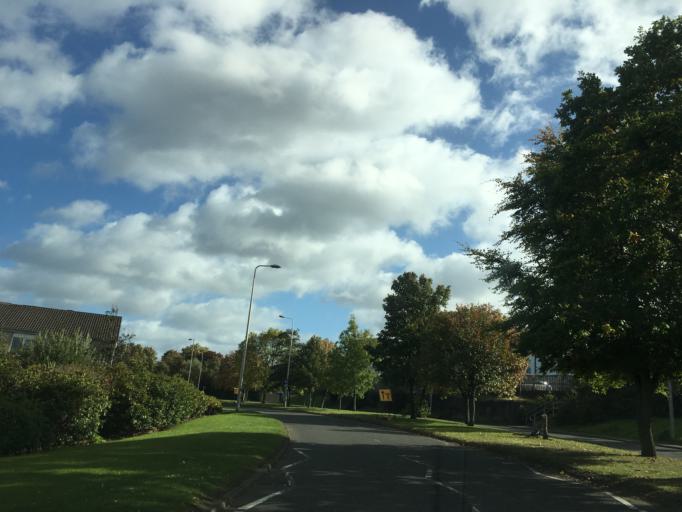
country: GB
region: Scotland
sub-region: Edinburgh
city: Currie
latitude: 55.9493
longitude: -3.3114
